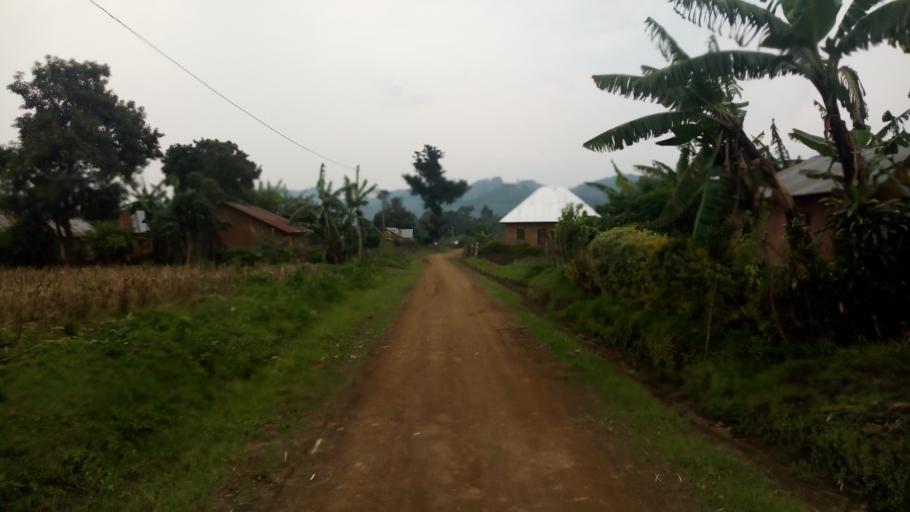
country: UG
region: Western Region
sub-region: Kisoro District
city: Kisoro
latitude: -1.2743
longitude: 29.6245
